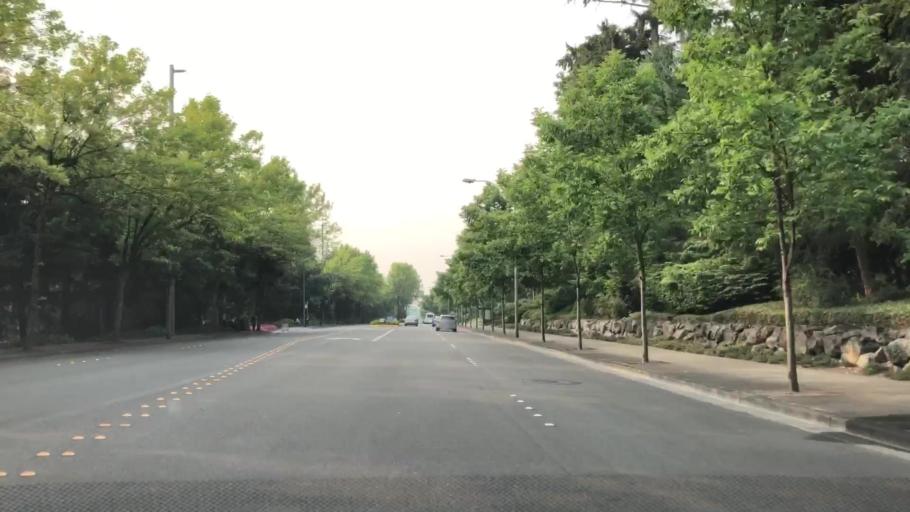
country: US
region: Washington
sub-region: King County
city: Redmond
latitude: 47.6530
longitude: -122.1325
